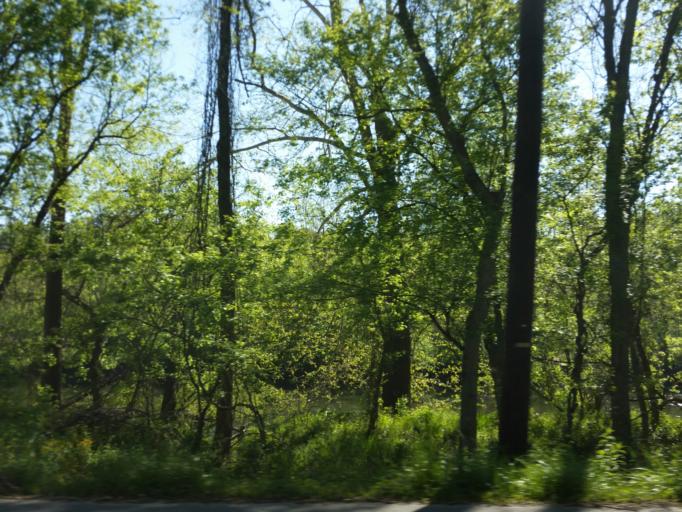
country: US
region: North Carolina
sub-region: Buncombe County
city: Asheville
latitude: 35.5735
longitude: -82.5649
